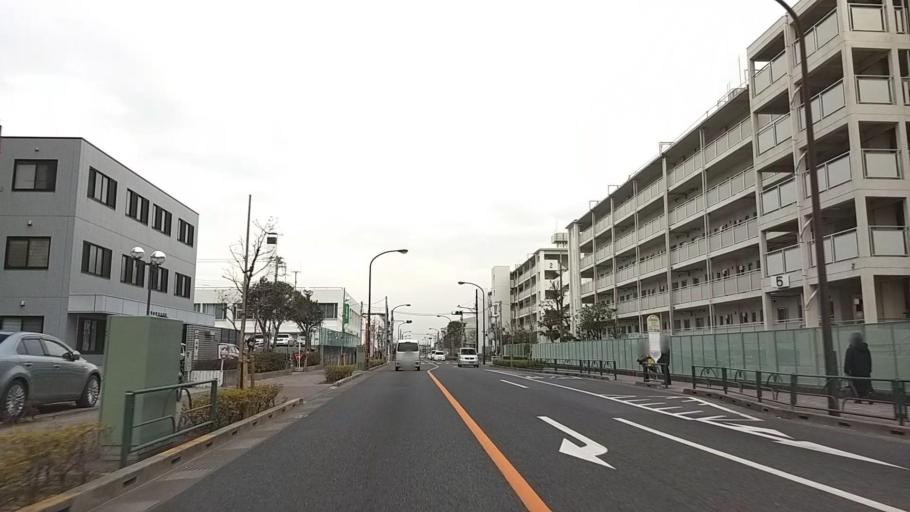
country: JP
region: Tokyo
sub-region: Machida-shi
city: Machida
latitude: 35.5545
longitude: 139.4441
